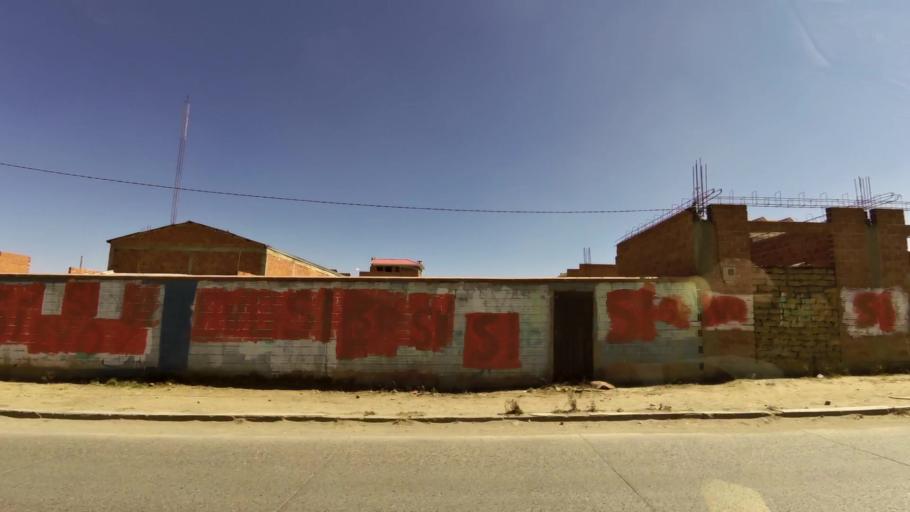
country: BO
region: La Paz
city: La Paz
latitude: -16.4986
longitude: -68.2076
